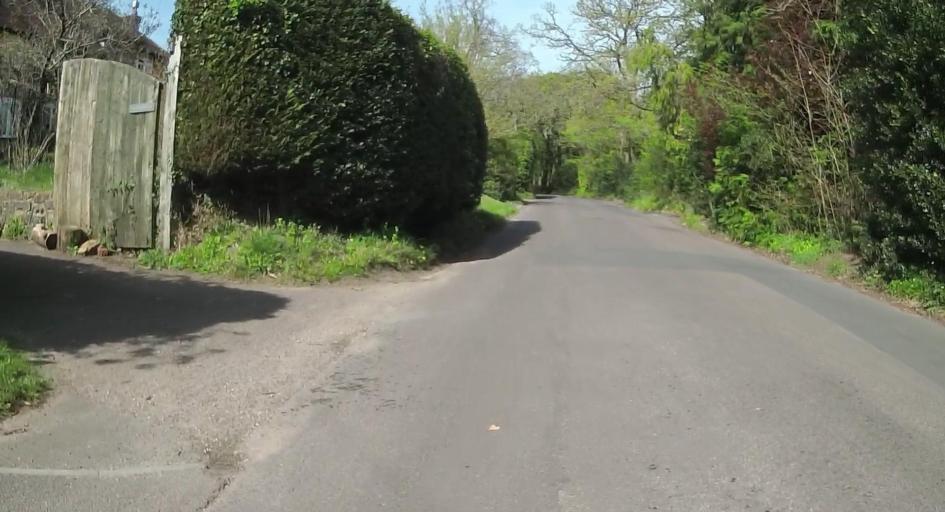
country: GB
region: England
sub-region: Surrey
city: Farnham
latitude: 51.1746
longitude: -0.7965
